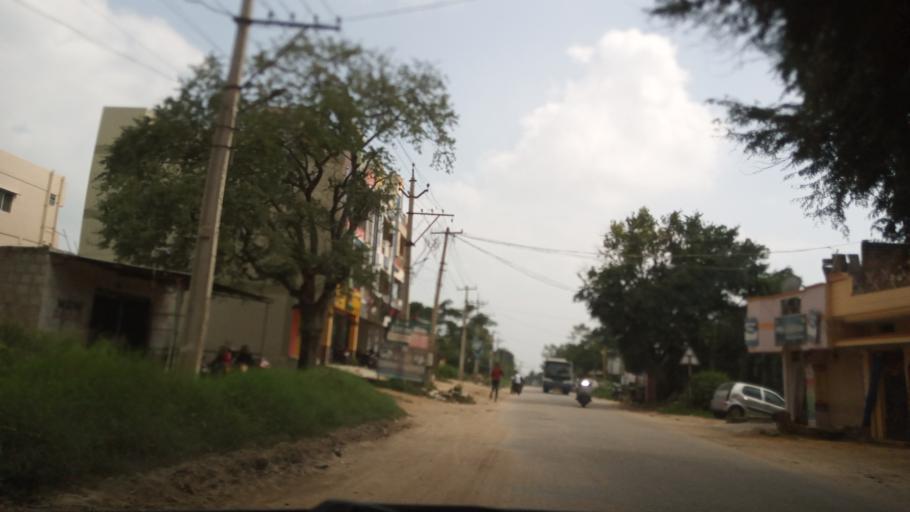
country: IN
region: Andhra Pradesh
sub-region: Chittoor
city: Madanapalle
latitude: 13.6392
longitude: 78.6346
